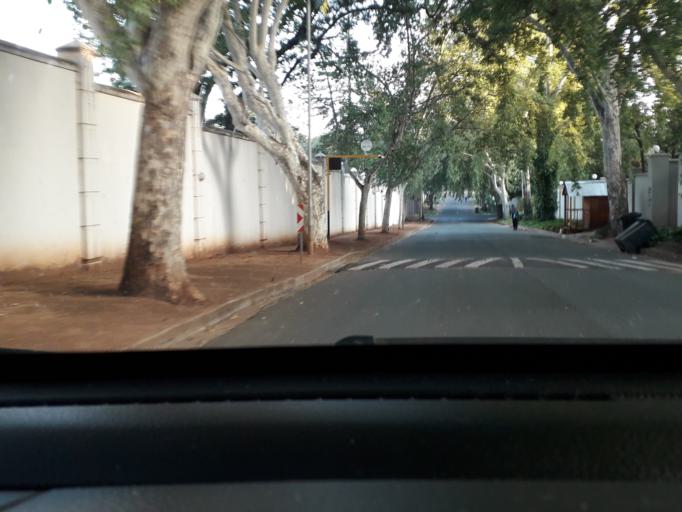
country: ZA
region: Gauteng
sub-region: City of Johannesburg Metropolitan Municipality
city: Johannesburg
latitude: -26.1568
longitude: 28.0515
